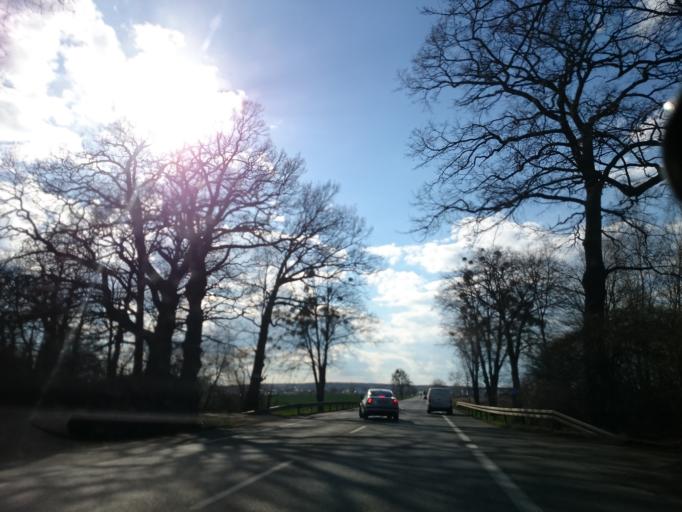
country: PL
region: Opole Voivodeship
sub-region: Powiat opolski
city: Dabrowa
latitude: 50.6899
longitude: 17.7721
